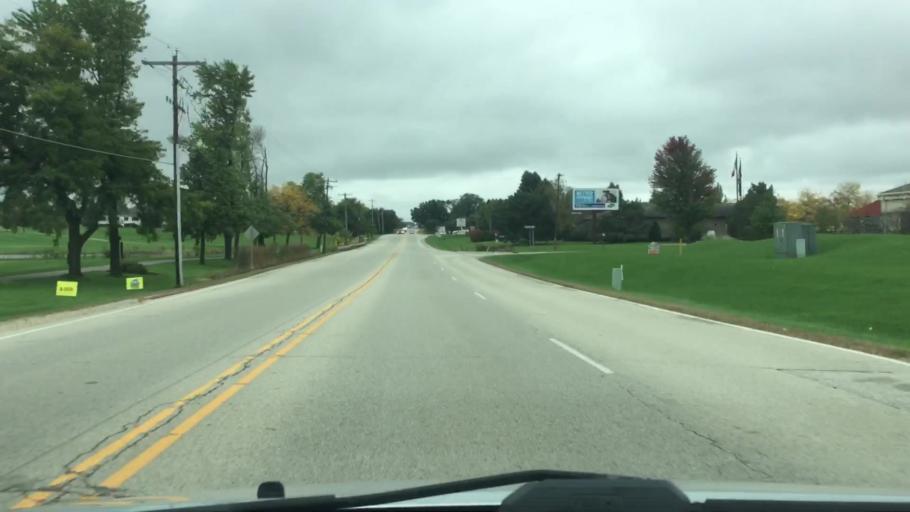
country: US
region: Wisconsin
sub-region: Walworth County
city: Elkhorn
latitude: 42.7181
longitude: -88.5425
